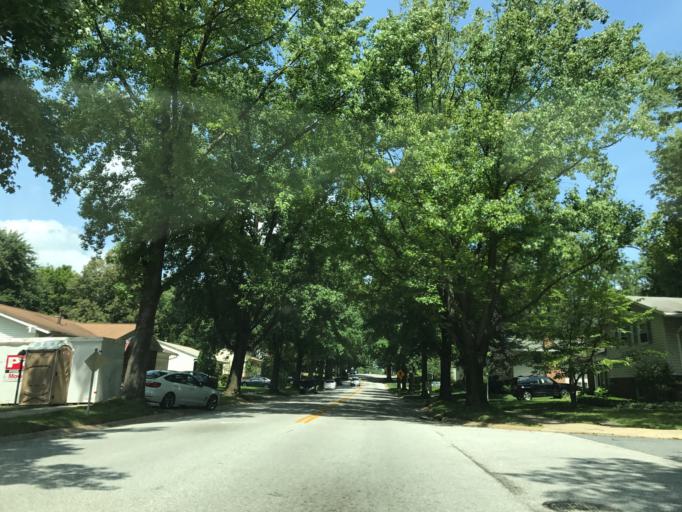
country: US
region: Maryland
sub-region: Howard County
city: Columbia
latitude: 39.2324
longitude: -76.8808
